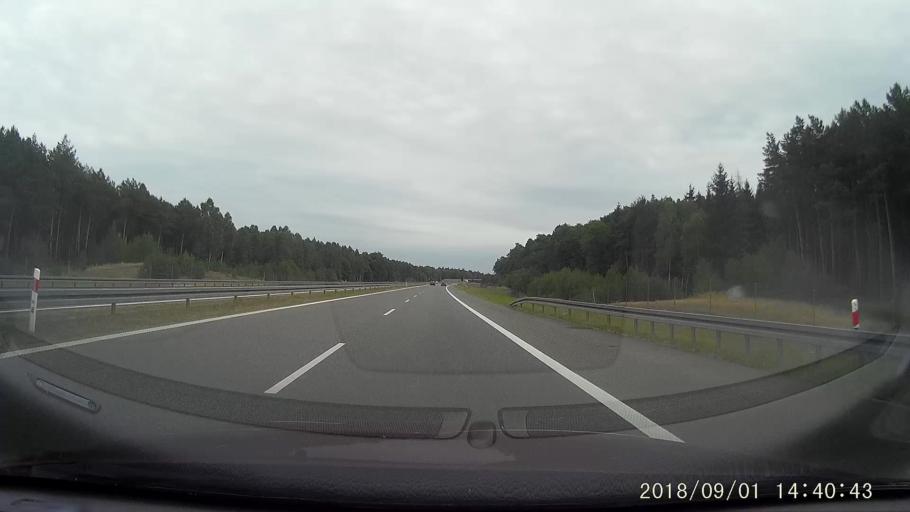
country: PL
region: Lubusz
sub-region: Powiat gorzowski
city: Jenin
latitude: 52.8029
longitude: 15.1067
